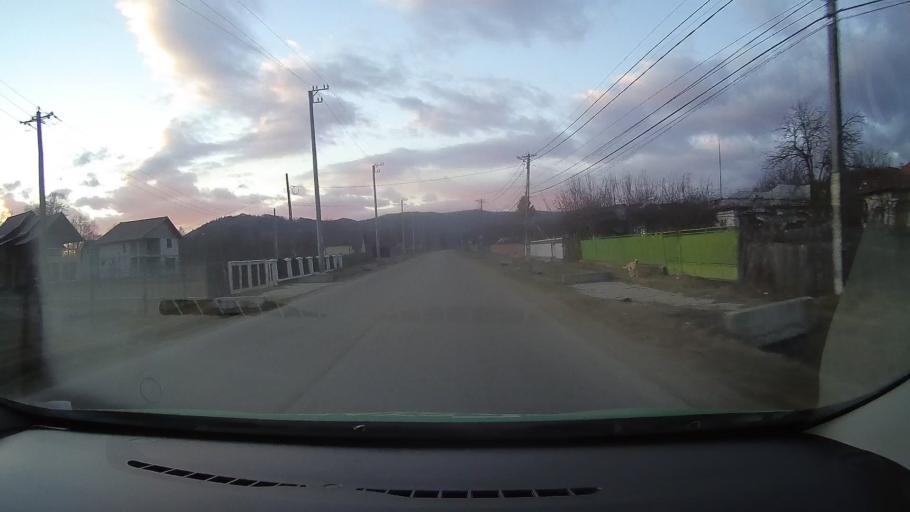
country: RO
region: Dambovita
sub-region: Comuna Valea Lunga
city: Valea Lunga-Cricov
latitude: 45.0643
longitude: 25.5869
